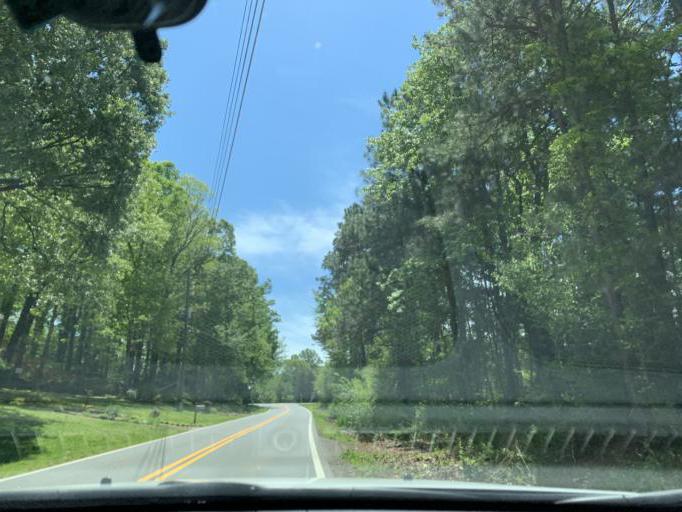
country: US
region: Georgia
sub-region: Hall County
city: Flowery Branch
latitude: 34.2569
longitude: -84.0233
